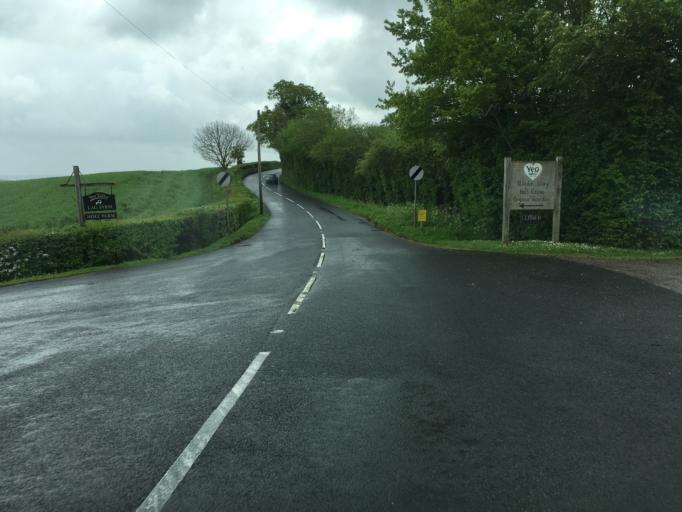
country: GB
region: England
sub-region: North Somerset
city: Blagdon
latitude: 51.3233
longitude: -2.6974
